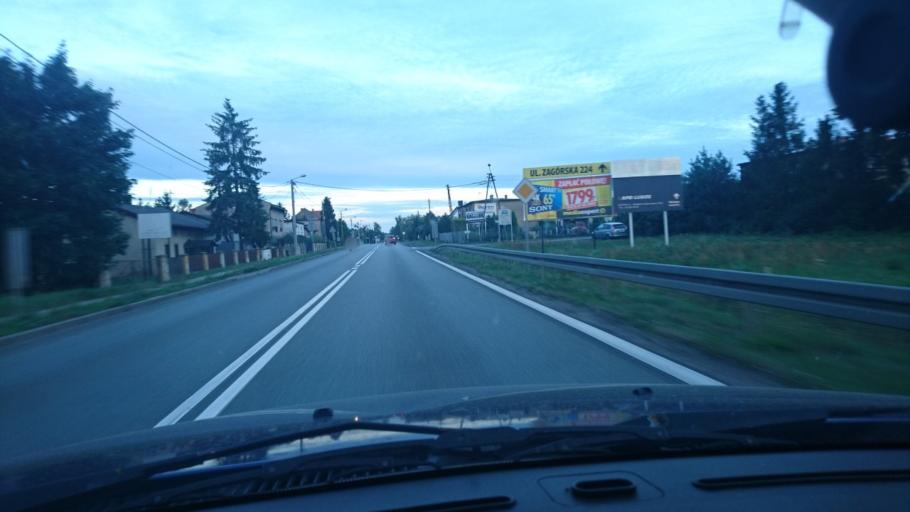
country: PL
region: Silesian Voivodeship
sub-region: Powiat tarnogorski
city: Tarnowskie Gory
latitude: 50.4709
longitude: 18.8058
